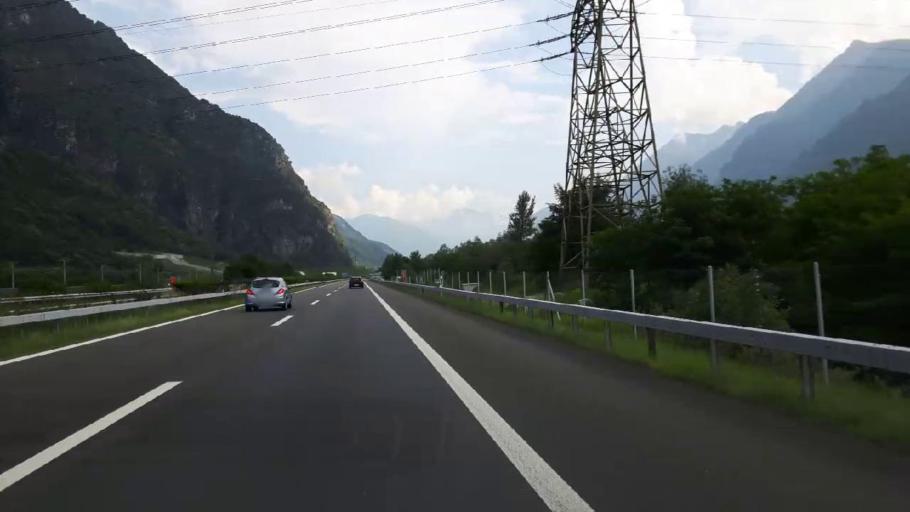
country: CH
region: Ticino
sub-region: Riviera District
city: Biasca
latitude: 46.3327
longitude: 8.9754
